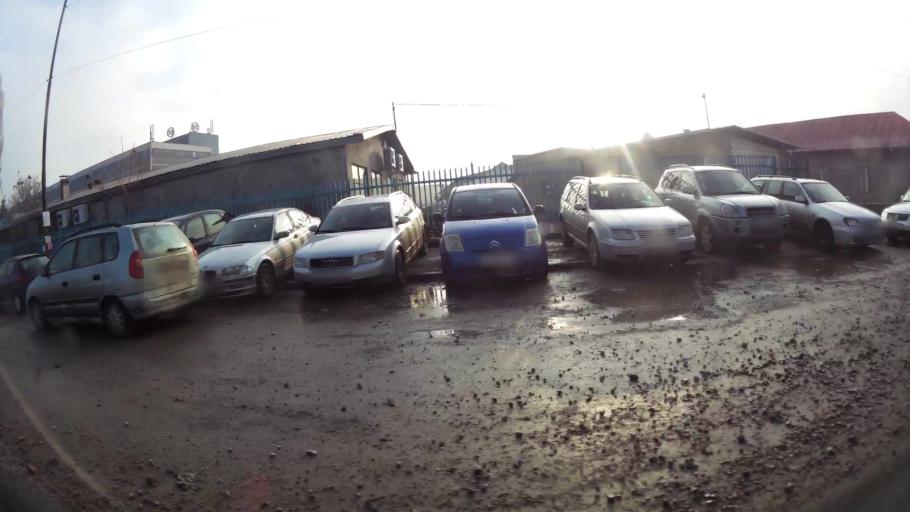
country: BG
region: Sofia-Capital
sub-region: Stolichna Obshtina
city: Sofia
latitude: 42.7279
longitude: 23.3184
